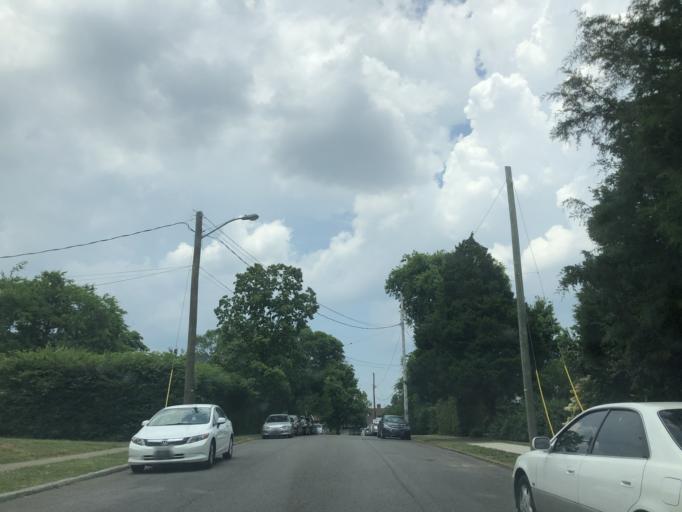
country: US
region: Tennessee
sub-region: Davidson County
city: Nashville
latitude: 36.1325
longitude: -86.8071
